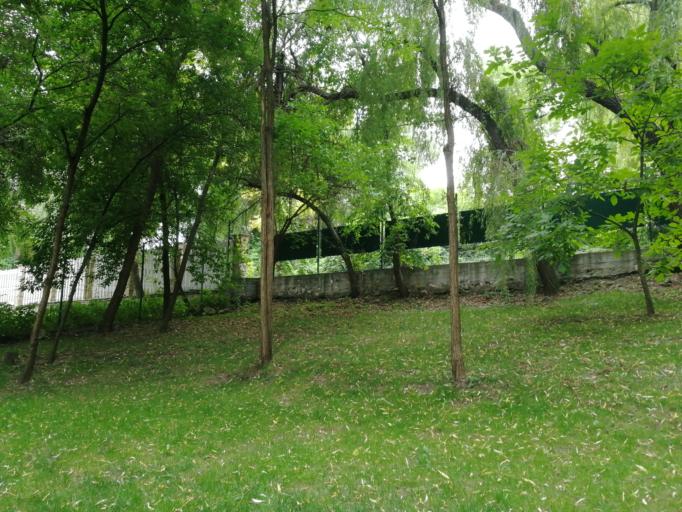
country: MD
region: Chisinau
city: Vatra
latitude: 47.1005
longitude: 28.7051
